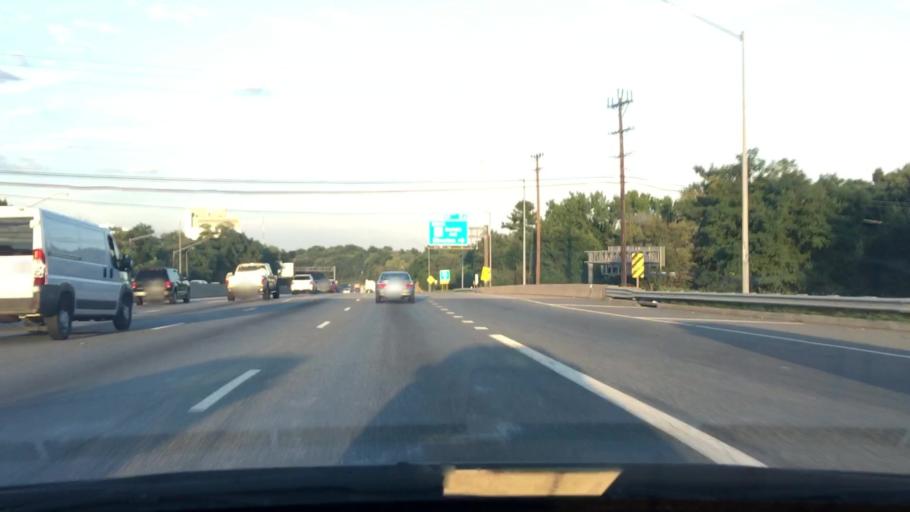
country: US
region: Maryland
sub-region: Montgomery County
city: Forest Glen
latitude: 39.0132
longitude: -77.0423
